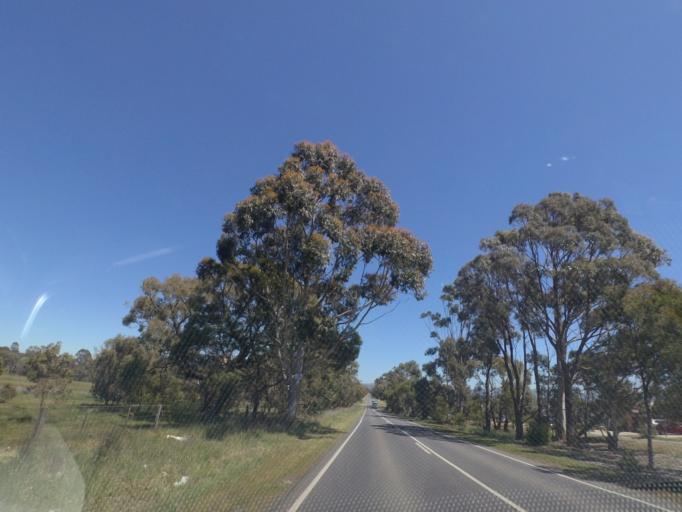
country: AU
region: Victoria
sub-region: Whittlesea
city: Whittlesea
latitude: -37.2938
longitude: 144.9313
